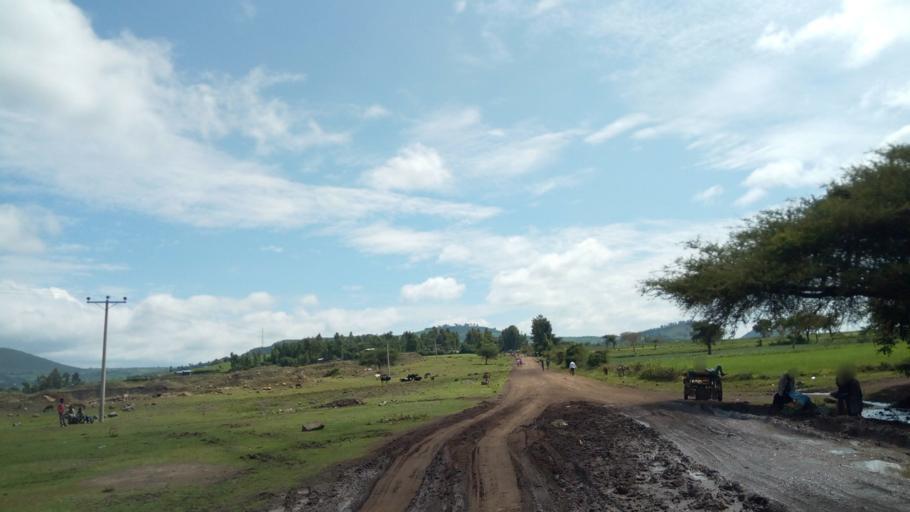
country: ET
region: Oromiya
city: Bishoftu
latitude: 8.8426
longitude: 39.0146
